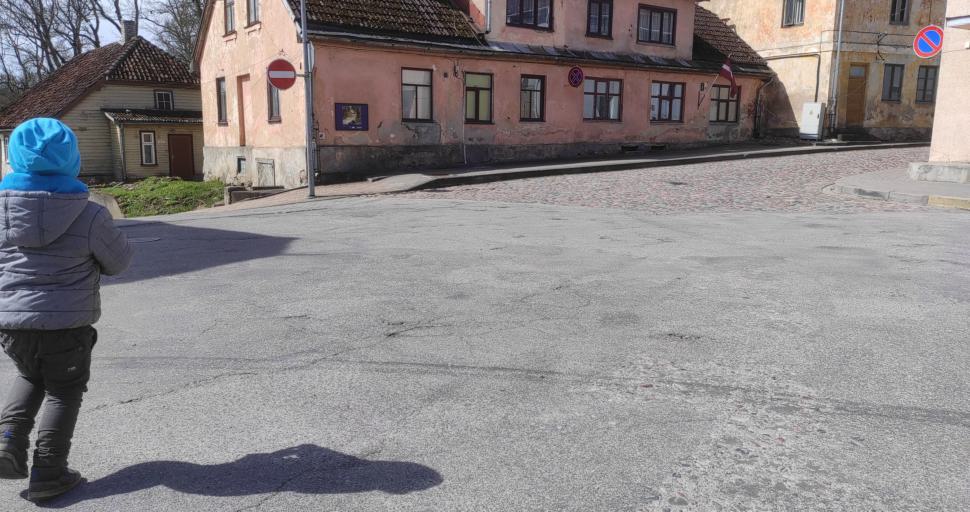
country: LV
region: Talsu Rajons
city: Talsi
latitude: 57.2452
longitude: 22.5975
